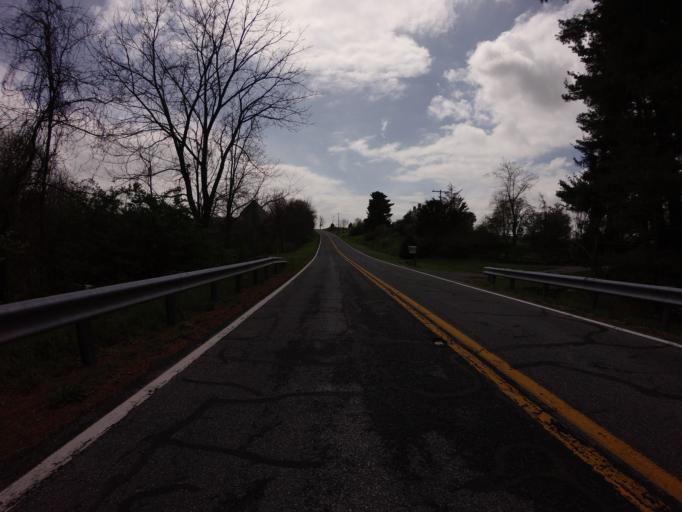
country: US
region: Maryland
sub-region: Frederick County
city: Emmitsburg
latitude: 39.6455
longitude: -77.3444
